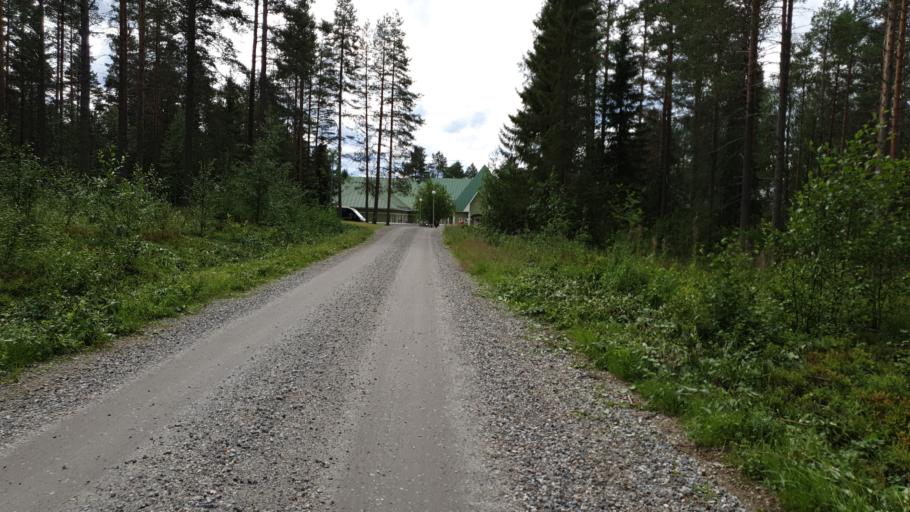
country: FI
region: Kainuu
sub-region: Kehys-Kainuu
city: Kuhmo
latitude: 64.3903
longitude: 29.8279
